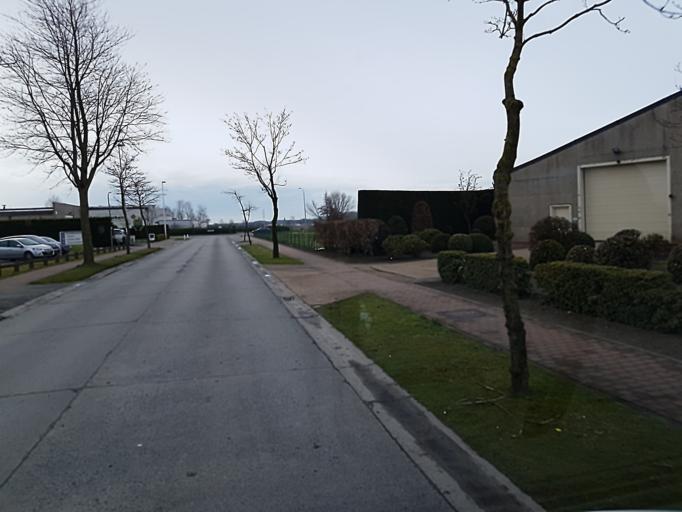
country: BE
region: Flanders
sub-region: Provincie Oost-Vlaanderen
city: Maldegem
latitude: 51.1970
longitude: 3.4658
